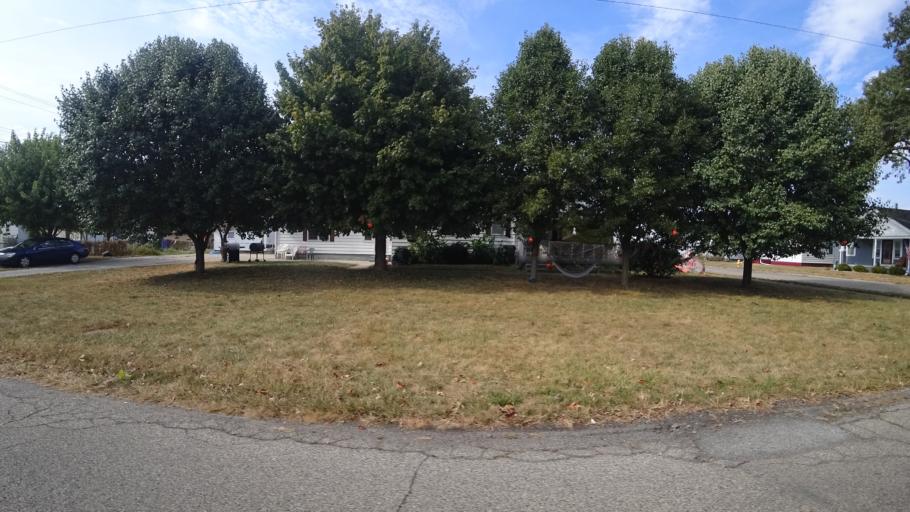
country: US
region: Ohio
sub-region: Butler County
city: Fairfield
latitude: 39.3617
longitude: -84.5530
